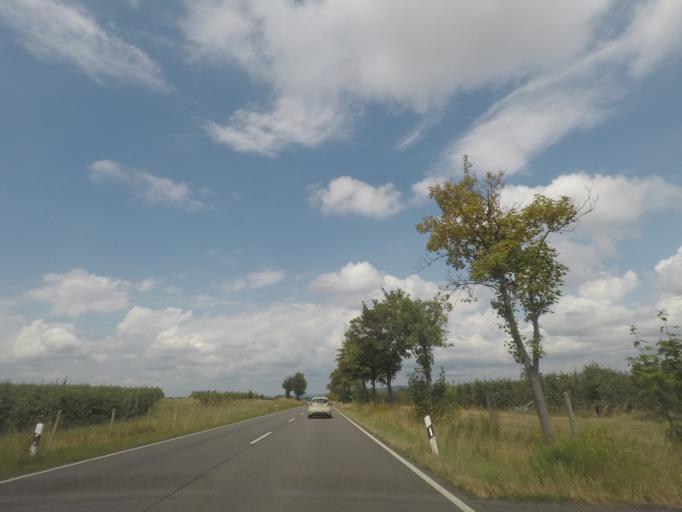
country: DE
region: Saxony
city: Pirna
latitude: 50.9408
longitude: 13.9632
